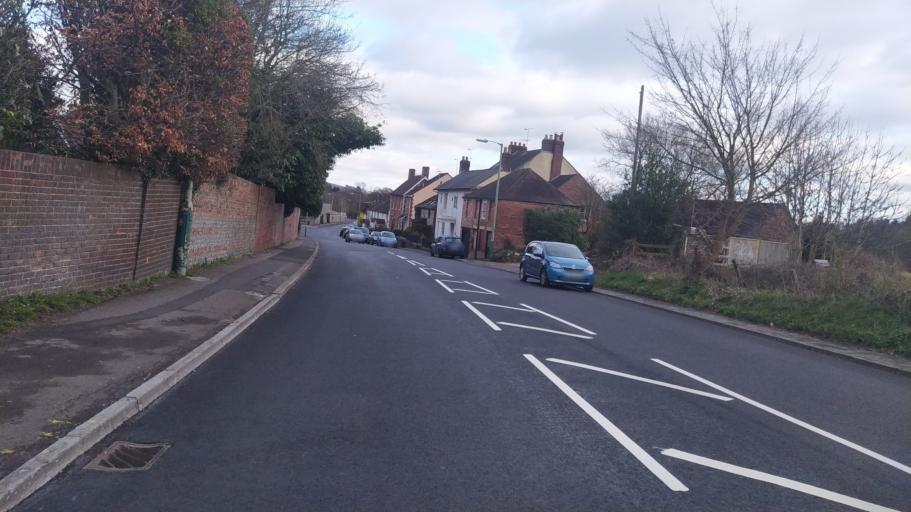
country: GB
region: England
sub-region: Wiltshire
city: Boreham
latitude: 51.1988
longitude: -2.1630
